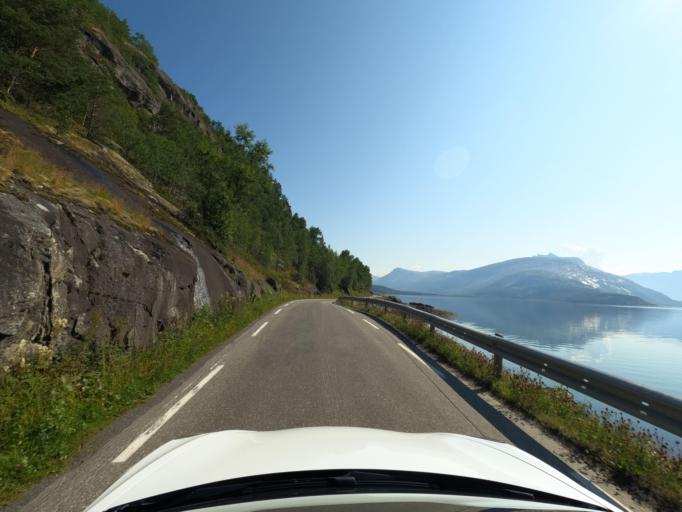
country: NO
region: Nordland
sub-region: Narvik
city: Narvik
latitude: 68.2878
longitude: 17.3676
